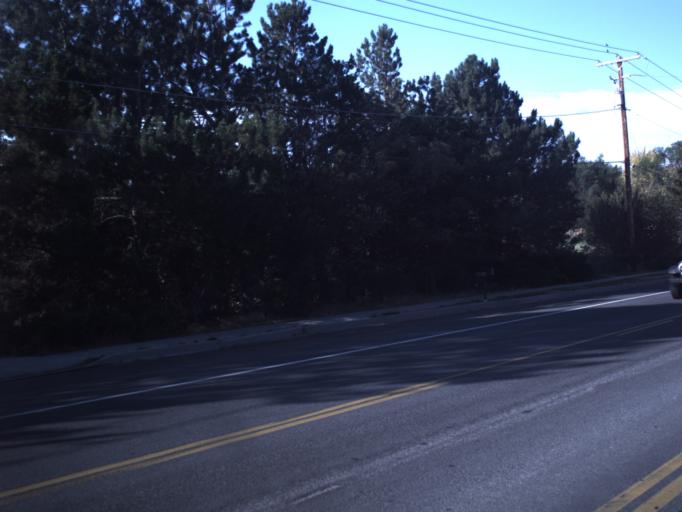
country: US
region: Utah
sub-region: Utah County
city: Alpine
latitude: 40.4472
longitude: -111.7795
